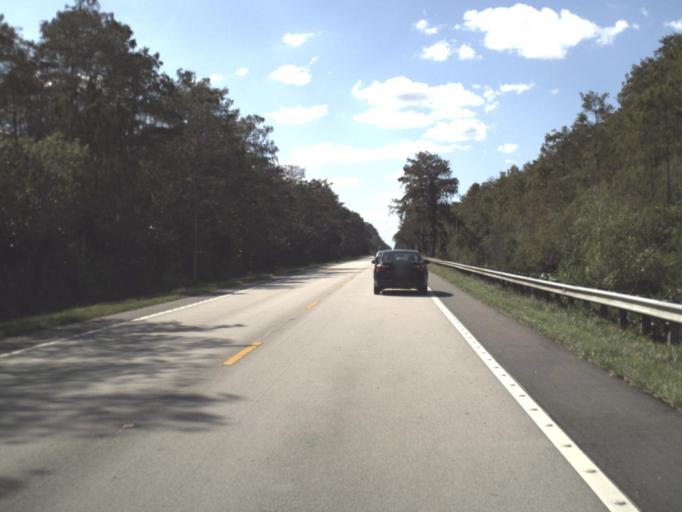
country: US
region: Florida
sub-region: Miami-Dade County
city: Kendall West
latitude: 25.8549
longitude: -81.0141
